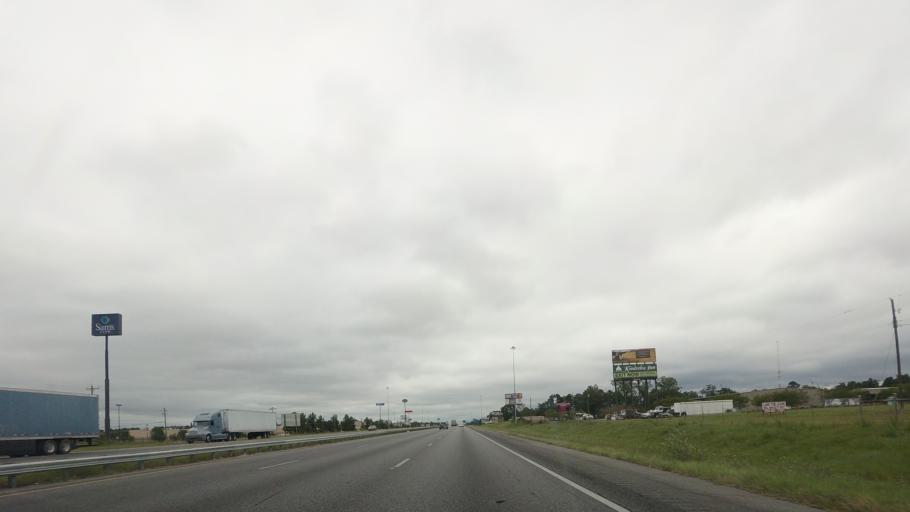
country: US
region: Georgia
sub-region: Lowndes County
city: Remerton
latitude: 30.8281
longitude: -83.3225
